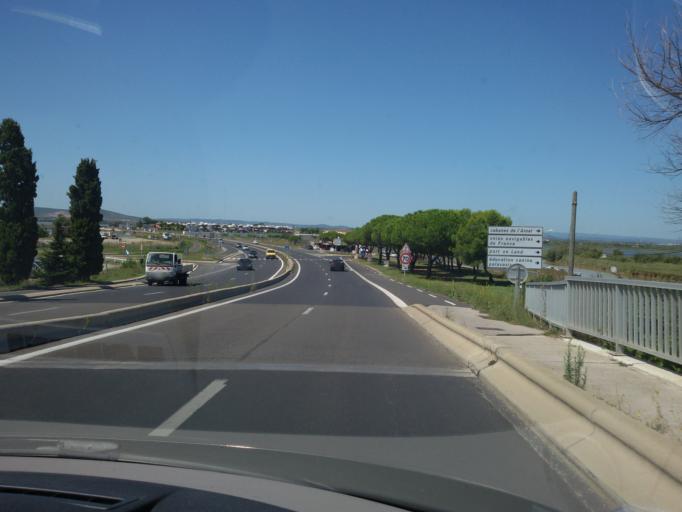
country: FR
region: Languedoc-Roussillon
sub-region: Departement de l'Herault
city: Palavas-les-Flots
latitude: 43.5344
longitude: 3.9160
